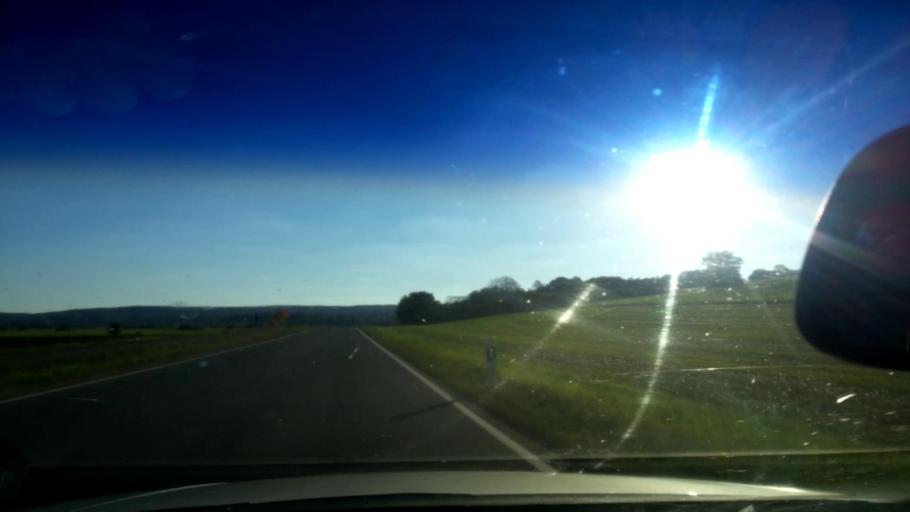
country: DE
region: Bavaria
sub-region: Upper Franconia
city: Baunach
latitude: 49.9984
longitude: 10.8704
